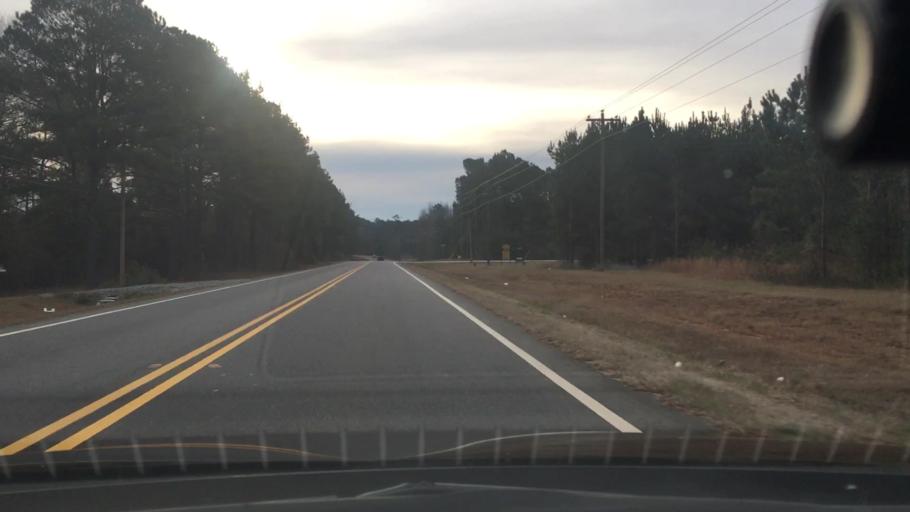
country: US
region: Georgia
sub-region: Coweta County
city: Senoia
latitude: 33.2667
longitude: -84.5223
